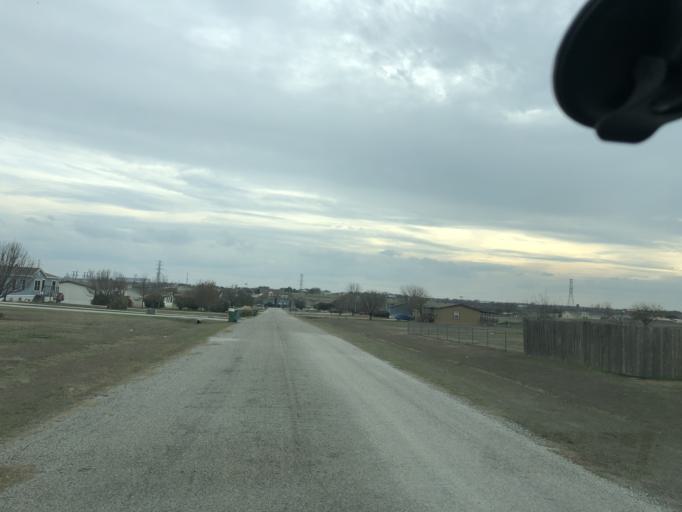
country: US
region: Texas
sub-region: Tarrant County
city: Saginaw
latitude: 32.9033
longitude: -97.3766
